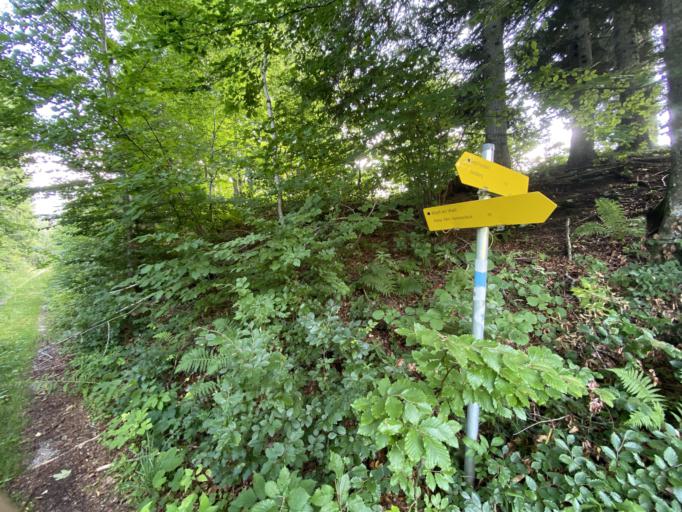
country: AT
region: Lower Austria
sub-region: Politischer Bezirk Lilienfeld
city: Annaberg
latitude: 47.8783
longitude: 15.3572
